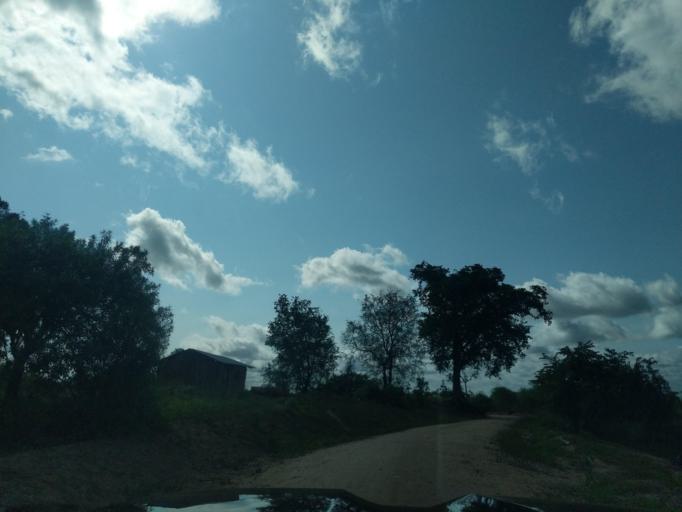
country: TZ
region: Tanga
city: Muheza
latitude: -5.4191
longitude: 38.6446
